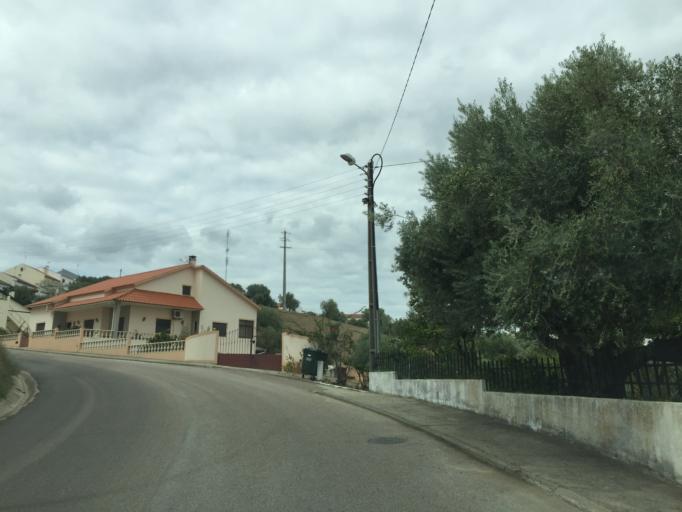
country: PT
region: Portalegre
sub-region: Ponte de Sor
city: Santo Andre
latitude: 39.0749
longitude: -8.1672
